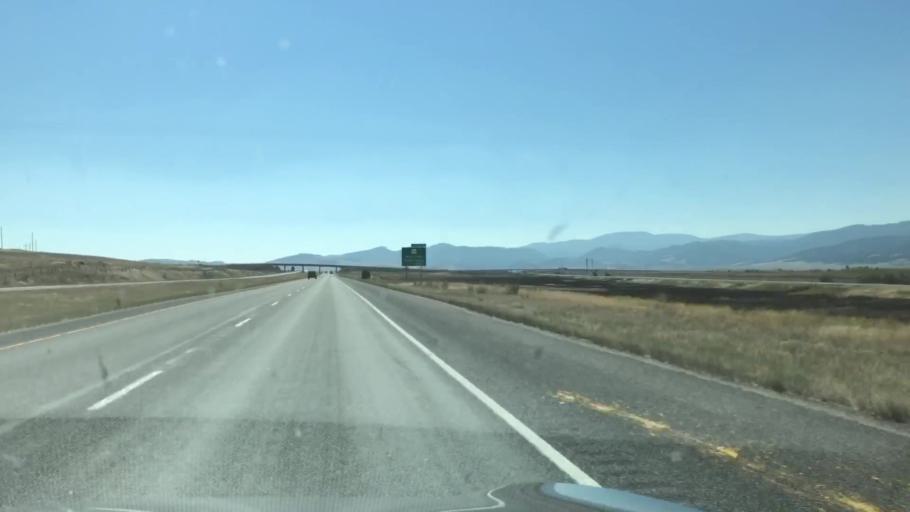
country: US
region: Montana
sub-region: Deer Lodge County
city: Warm Springs
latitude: 46.1148
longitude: -112.8004
